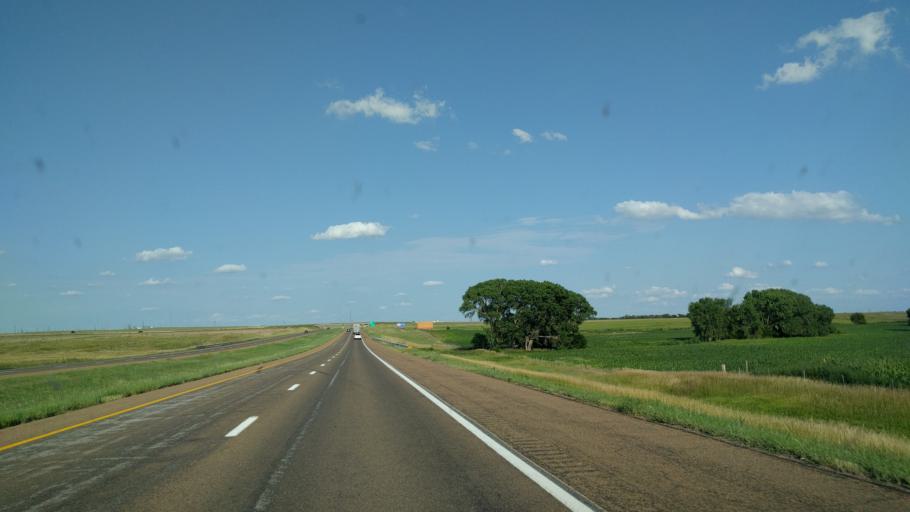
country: US
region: Kansas
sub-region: Ellis County
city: Hays
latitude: 38.9216
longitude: -99.4013
